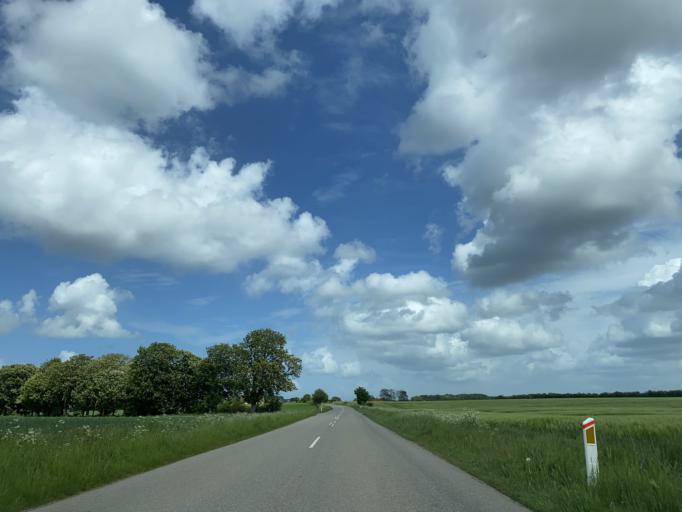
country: DK
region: South Denmark
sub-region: Sonderborg Kommune
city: Dybbol
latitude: 54.9713
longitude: 9.7107
